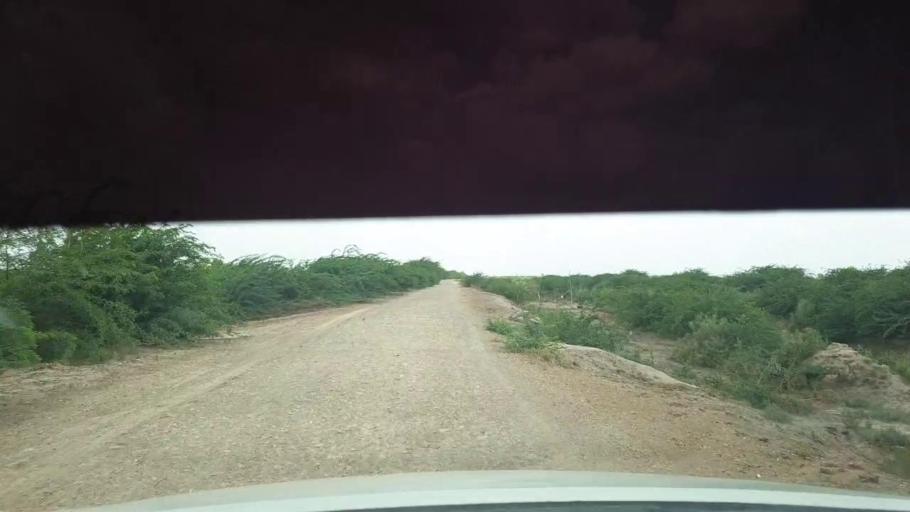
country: PK
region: Sindh
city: Kadhan
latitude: 24.4775
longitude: 69.0657
